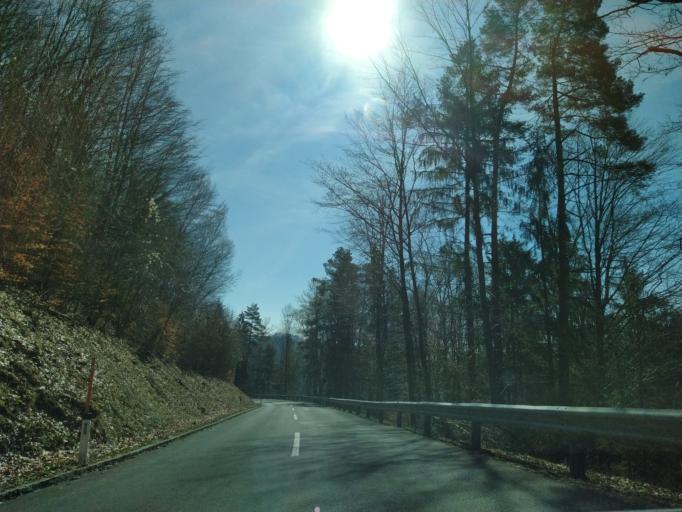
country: AT
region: Upper Austria
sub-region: Politischer Bezirk Urfahr-Umgebung
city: Kirchschlag bei Linz
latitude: 48.3874
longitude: 14.2872
